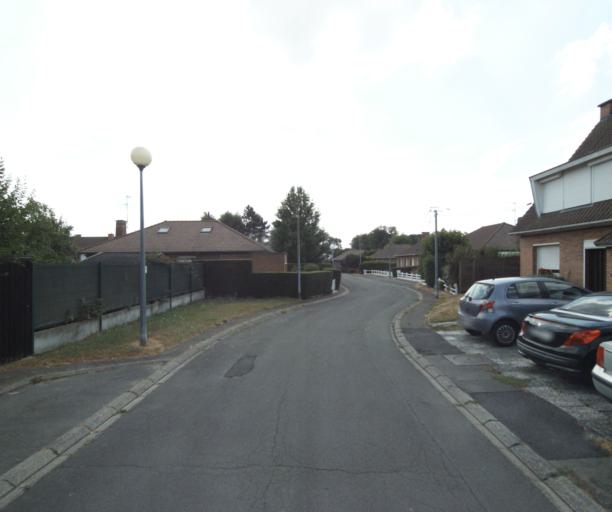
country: FR
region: Nord-Pas-de-Calais
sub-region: Departement du Nord
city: Neuville-en-Ferrain
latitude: 50.7448
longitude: 3.1639
